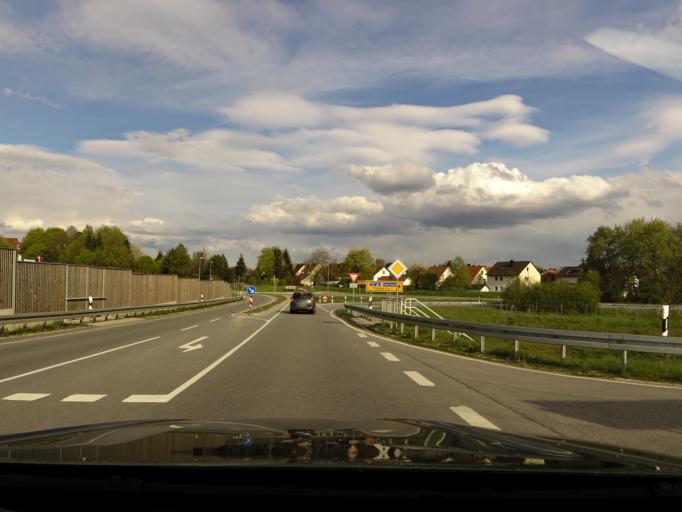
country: DE
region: Bavaria
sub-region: Upper Bavaria
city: Moosburg
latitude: 48.4598
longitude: 11.9209
